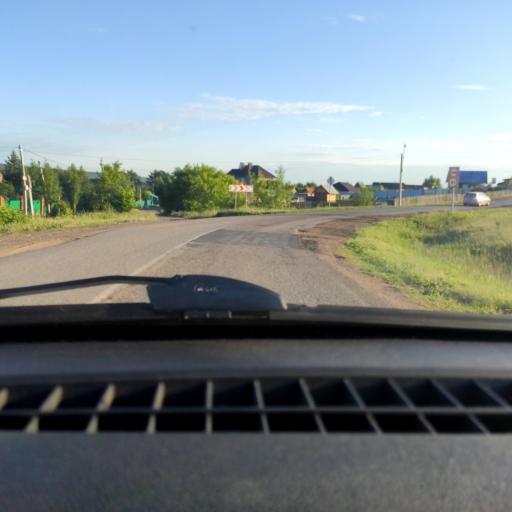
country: RU
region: Bashkortostan
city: Avdon
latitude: 54.6280
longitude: 55.6929
